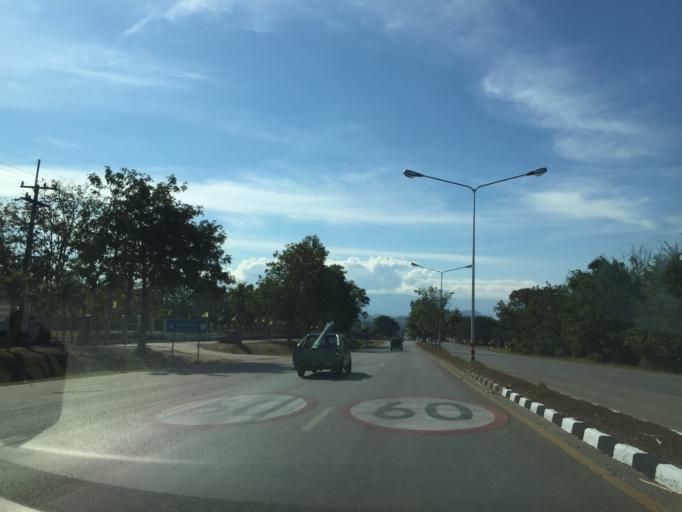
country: TH
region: Loei
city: Wang Saphung
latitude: 17.3019
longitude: 101.7921
